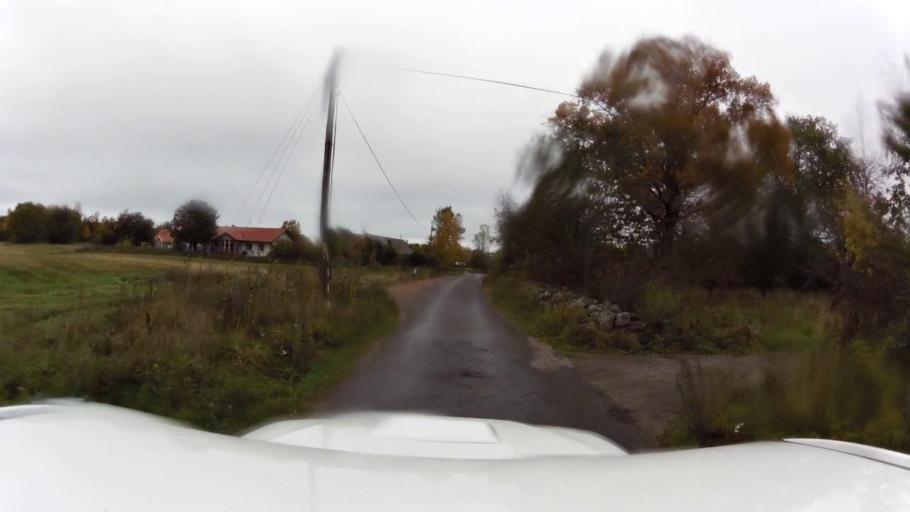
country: SE
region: OEstergoetland
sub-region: Linkopings Kommun
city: Linghem
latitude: 58.4942
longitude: 15.7430
